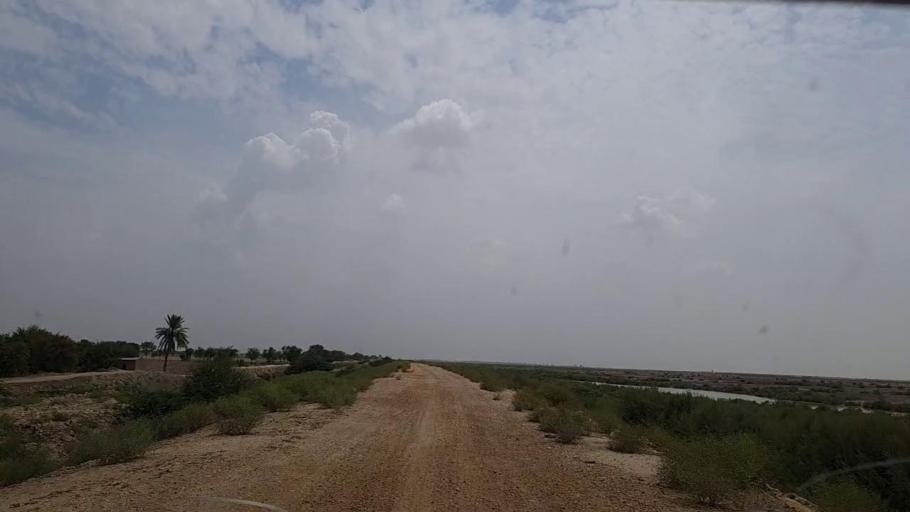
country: PK
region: Sindh
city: Phulji
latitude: 26.8031
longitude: 67.6035
